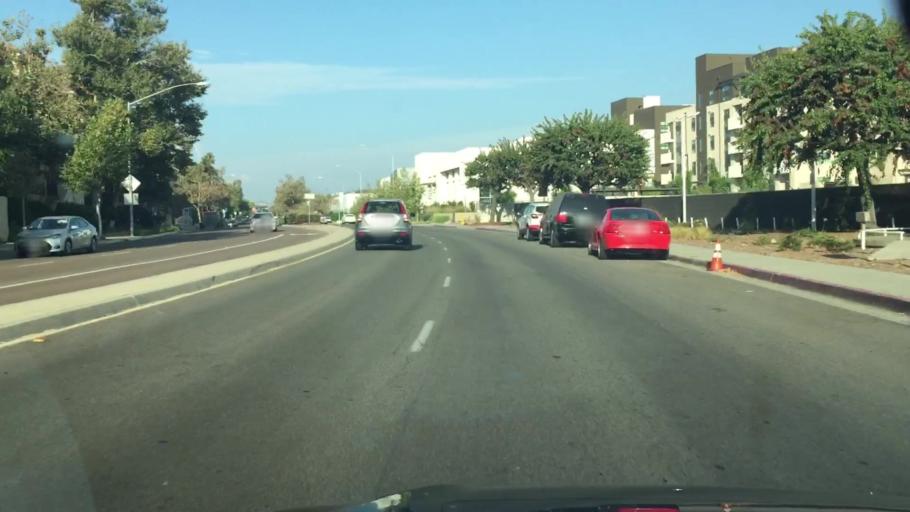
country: US
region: California
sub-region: San Diego County
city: San Diego
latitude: 32.7664
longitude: -117.1603
